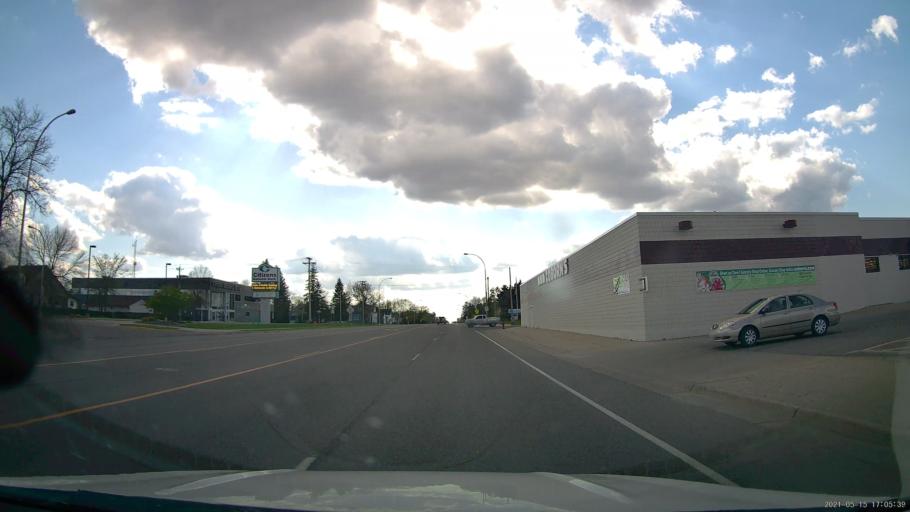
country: US
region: Minnesota
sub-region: Hubbard County
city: Park Rapids
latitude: 46.9222
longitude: -95.0611
